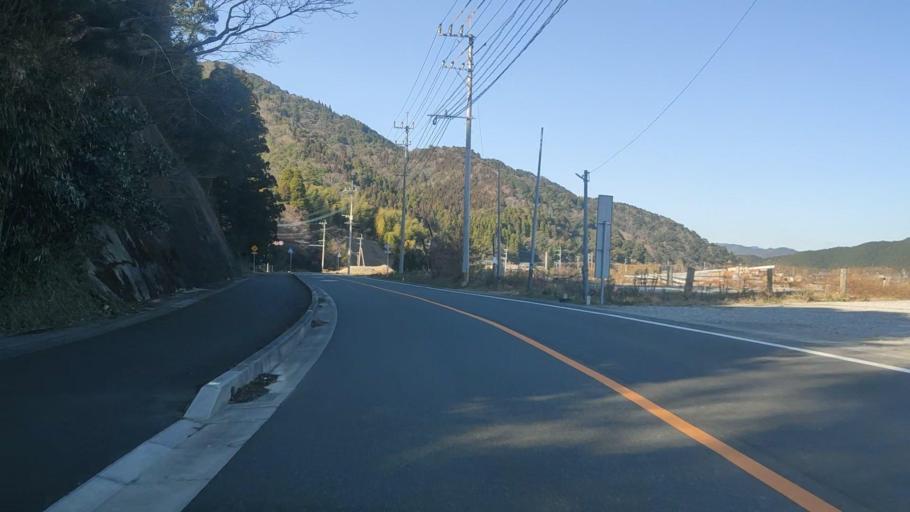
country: JP
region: Oita
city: Saiki
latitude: 32.9248
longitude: 131.9258
